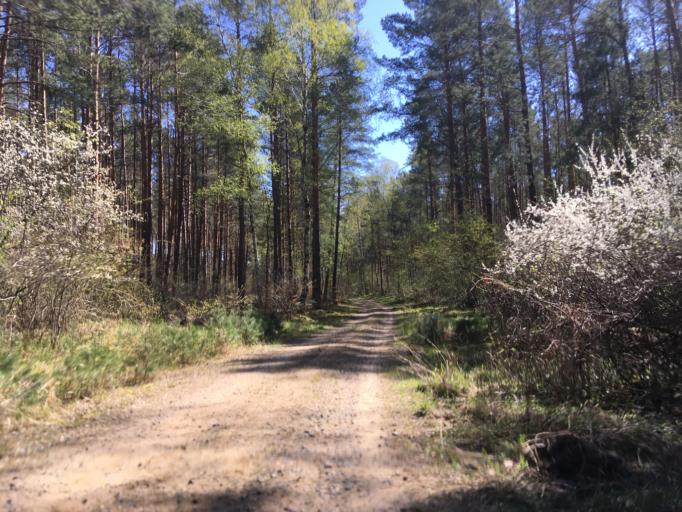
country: DE
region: Brandenburg
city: Bernau bei Berlin
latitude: 52.7036
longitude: 13.5233
